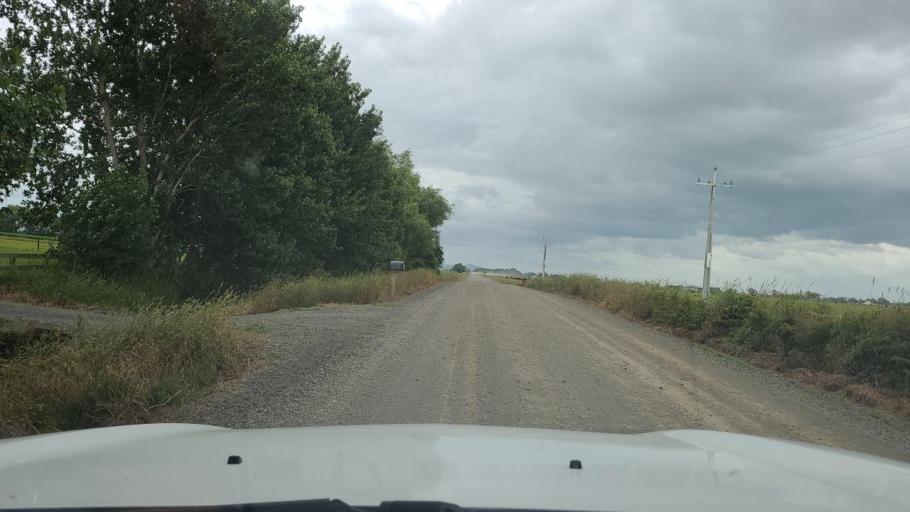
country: NZ
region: Waikato
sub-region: Hamilton City
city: Hamilton
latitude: -37.6272
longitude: 175.4272
